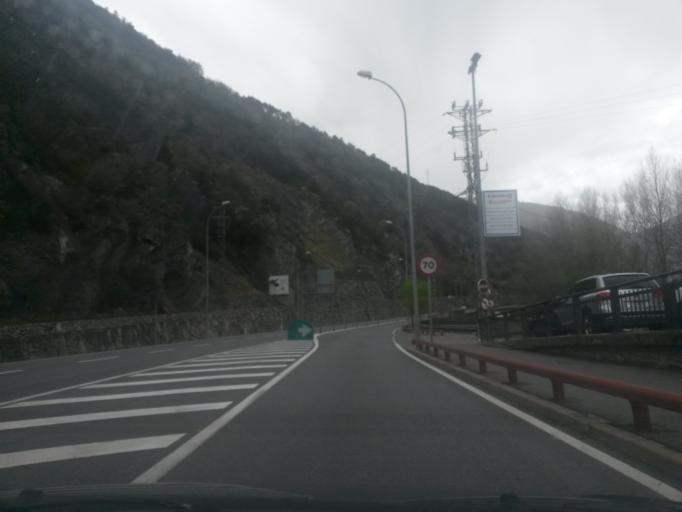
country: AD
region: Sant Julia de Loria
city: Sant Julia de Loria
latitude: 42.4465
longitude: 1.4821
